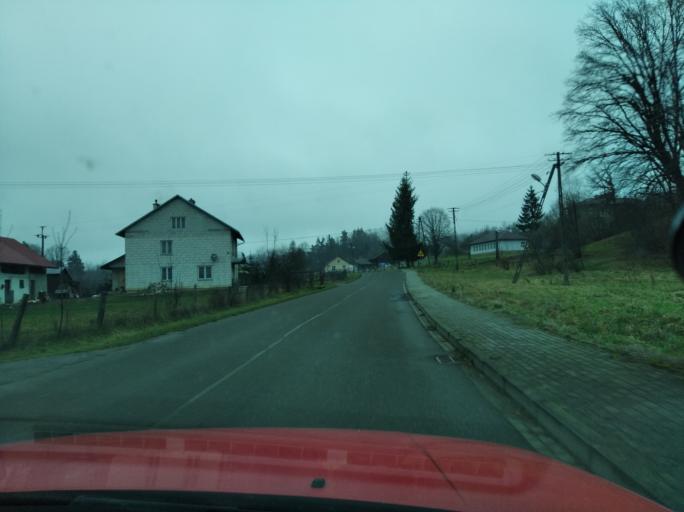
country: PL
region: Subcarpathian Voivodeship
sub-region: Powiat przemyski
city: Nienadowa
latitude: 49.8364
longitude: 22.4335
